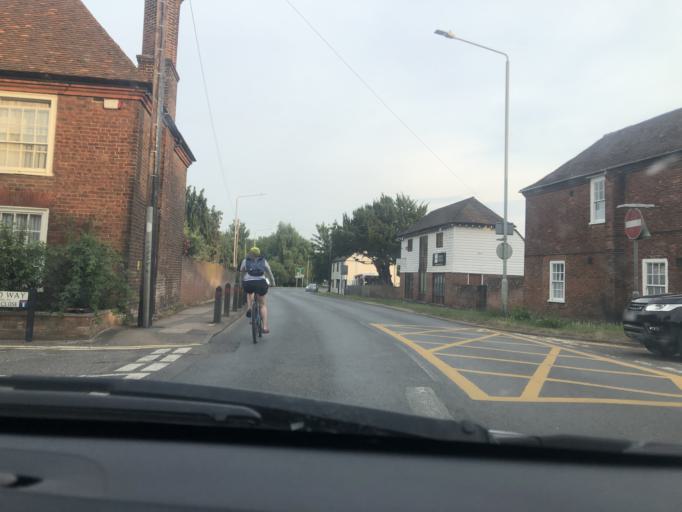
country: GB
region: England
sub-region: Kent
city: Sturry
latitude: 51.3006
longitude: 1.1221
